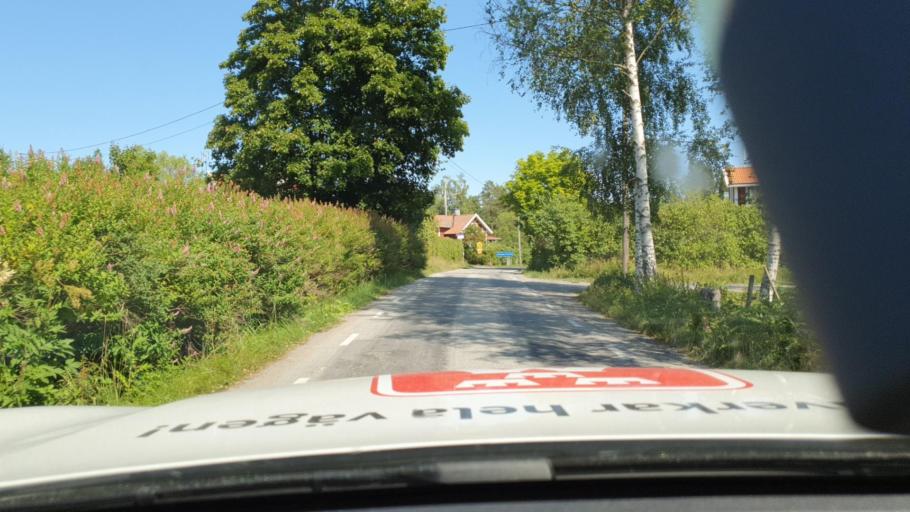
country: SE
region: Stockholm
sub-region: Norrtalje Kommun
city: Bjorko
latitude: 59.8129
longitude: 18.9737
